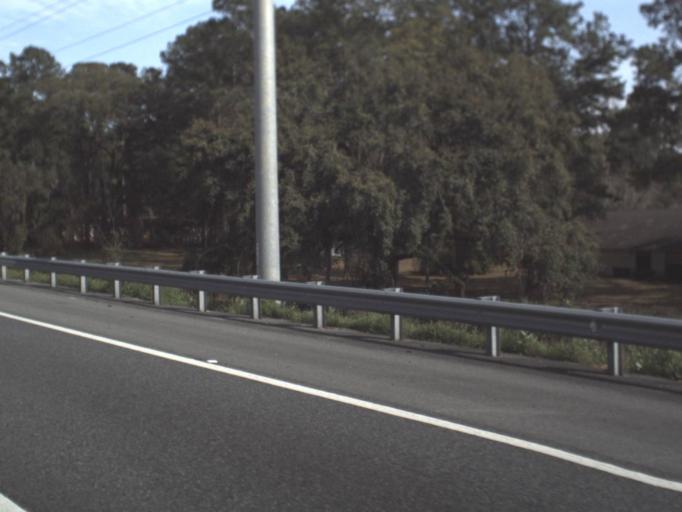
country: US
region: Florida
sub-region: Leon County
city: Tallahassee
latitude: 30.4807
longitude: -84.3165
